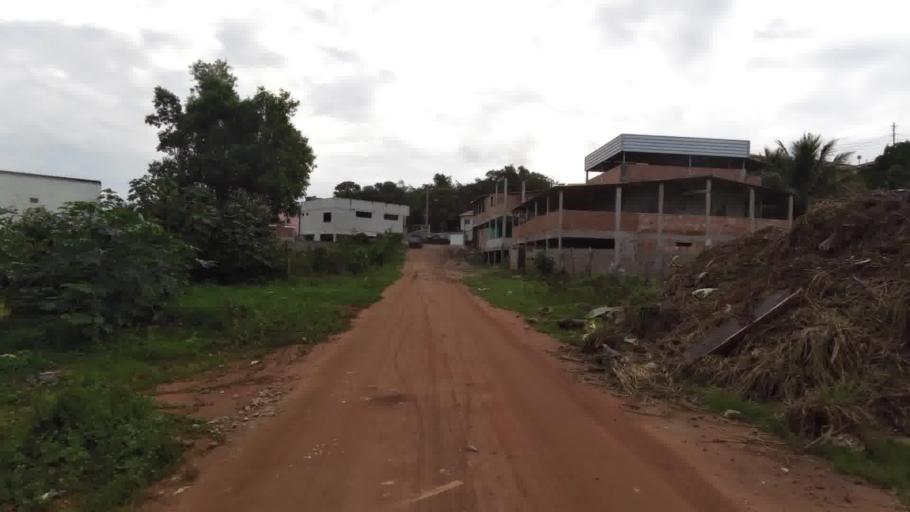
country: BR
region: Espirito Santo
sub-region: Piuma
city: Piuma
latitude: -20.8034
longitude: -40.6468
